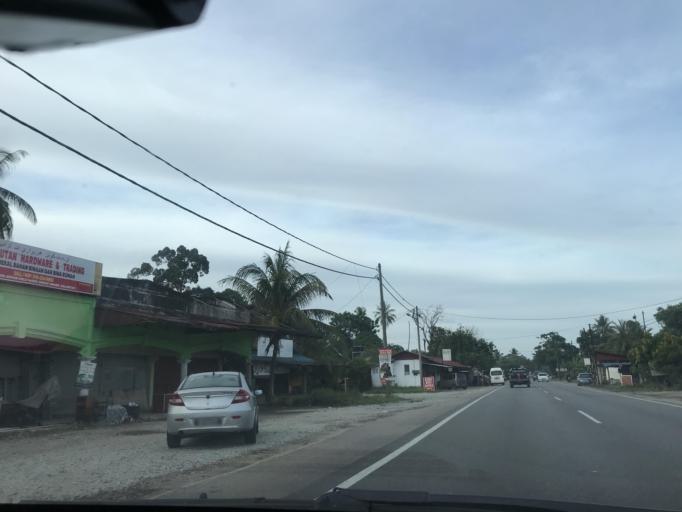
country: MY
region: Kelantan
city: Kota Bharu
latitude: 6.0949
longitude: 102.2087
